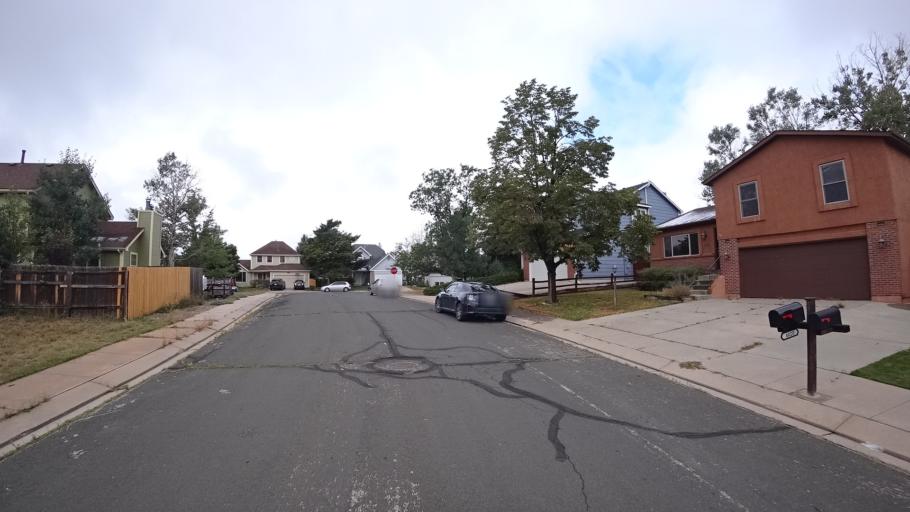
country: US
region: Colorado
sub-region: El Paso County
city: Cimarron Hills
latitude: 38.9232
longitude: -104.7528
